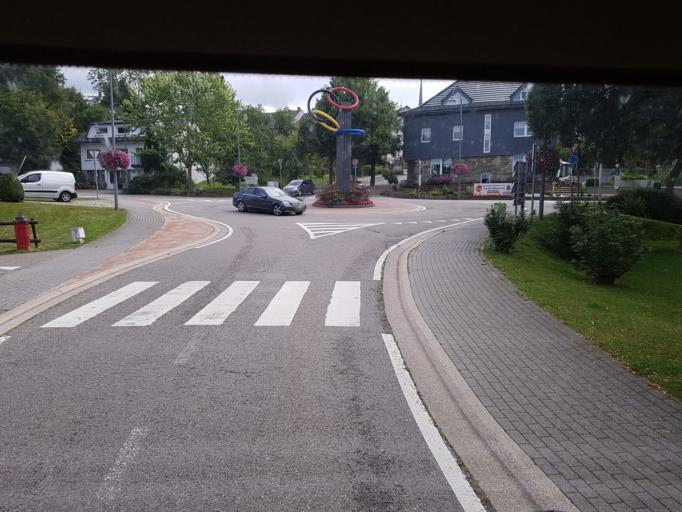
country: BE
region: Wallonia
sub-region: Province de Liege
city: Saint-Vith
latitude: 50.2810
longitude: 6.1227
